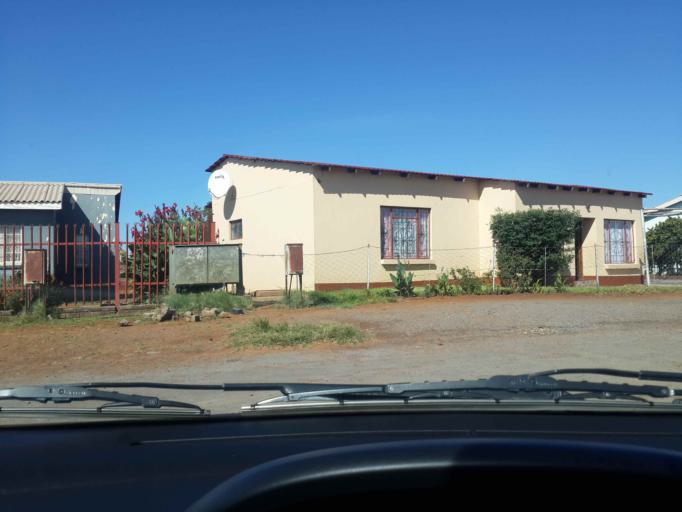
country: ZA
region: Northern Cape
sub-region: Siyanda District Municipality
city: Danielskuil
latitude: -28.1931
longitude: 23.5377
